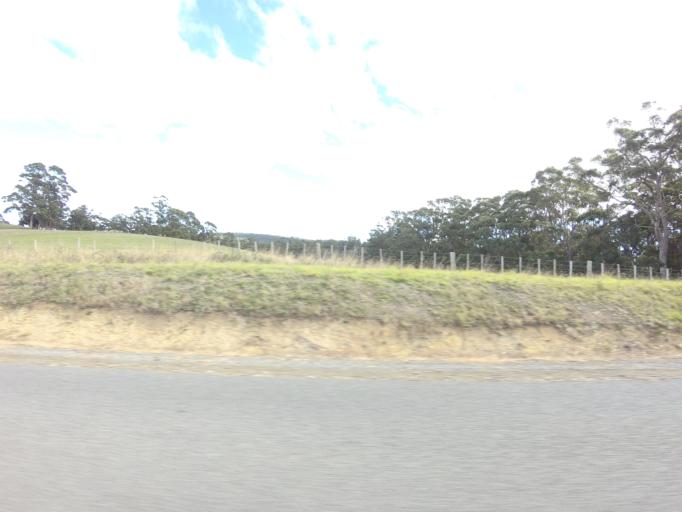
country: AU
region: Tasmania
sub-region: Clarence
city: Sandford
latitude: -43.0758
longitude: 147.7492
